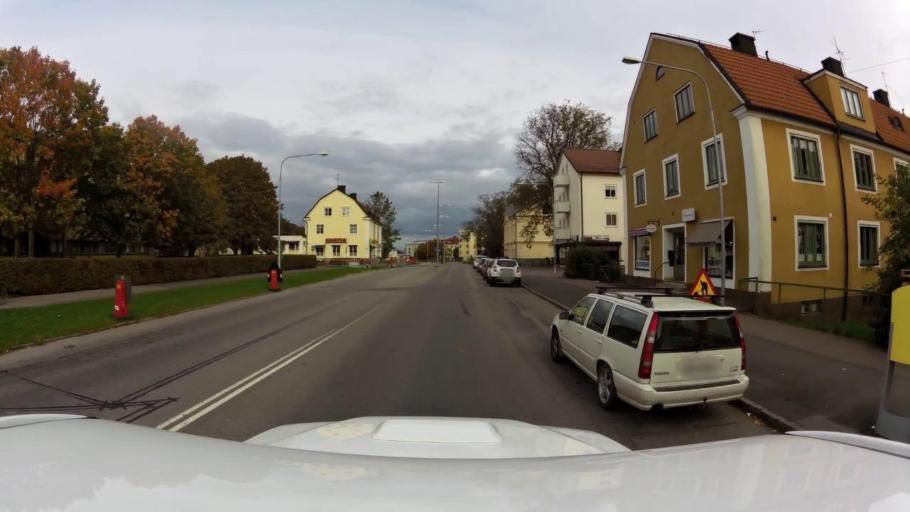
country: SE
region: OEstergoetland
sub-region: Linkopings Kommun
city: Linkoping
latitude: 58.4130
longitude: 15.6065
